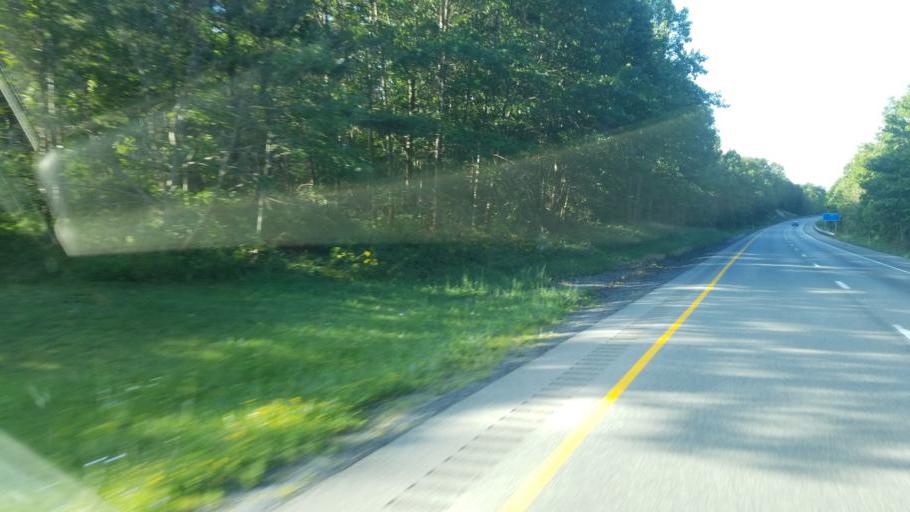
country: US
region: Pennsylvania
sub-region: Bedford County
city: Earlston
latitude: 39.9039
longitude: -78.2389
